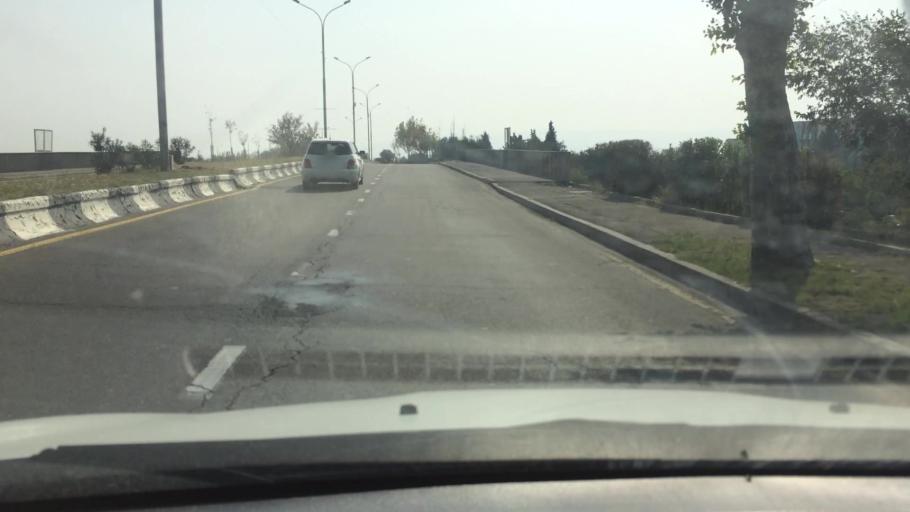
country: GE
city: Didi Lilo
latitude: 41.6873
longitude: 44.9531
